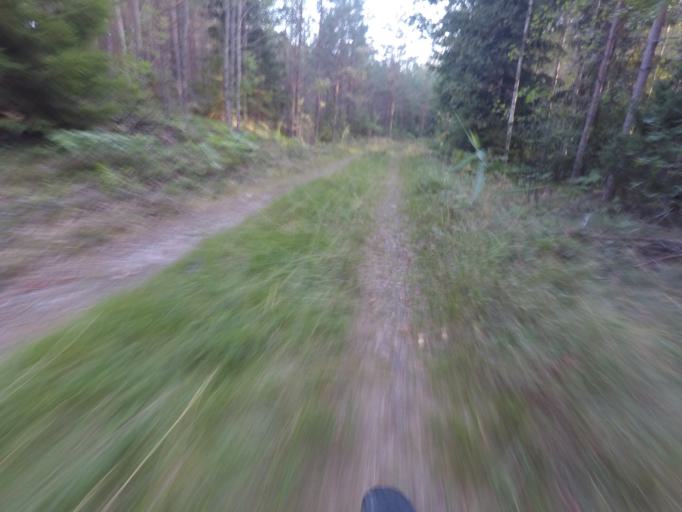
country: SE
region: Soedermanland
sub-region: Eskilstuna Kommun
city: Kvicksund
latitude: 59.4179
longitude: 16.3162
